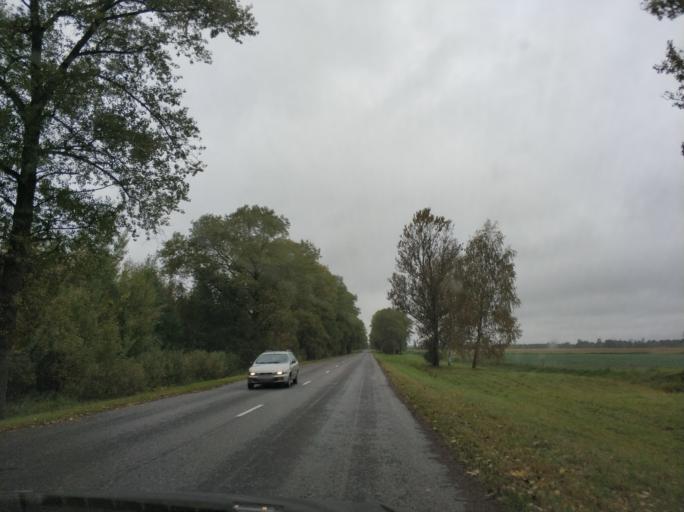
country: BY
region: Vitebsk
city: Polatsk
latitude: 55.4335
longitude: 28.9836
